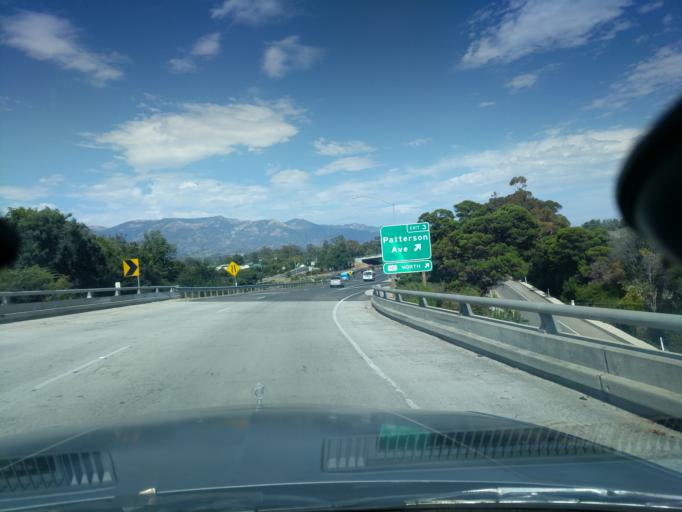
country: US
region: California
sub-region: Santa Barbara County
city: Goleta
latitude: 34.4411
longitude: -119.8128
